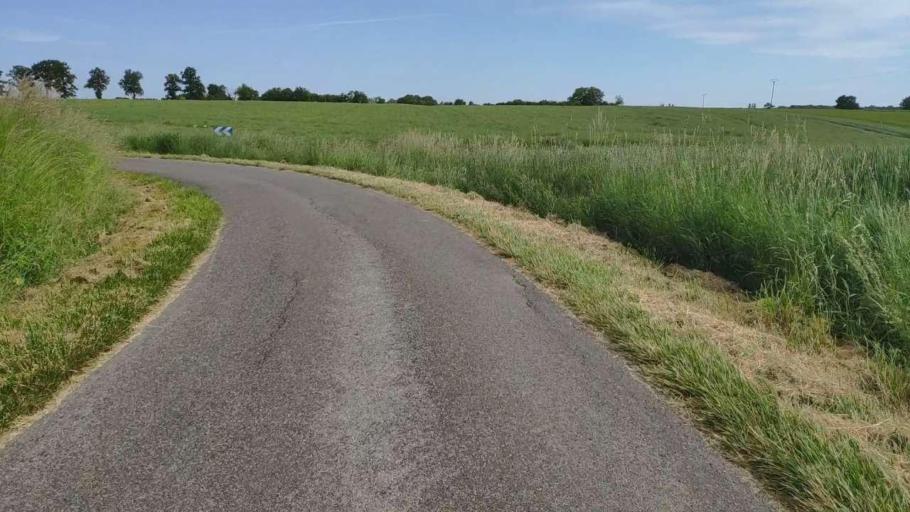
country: FR
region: Franche-Comte
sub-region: Departement du Jura
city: Bletterans
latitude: 46.6859
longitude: 5.4097
